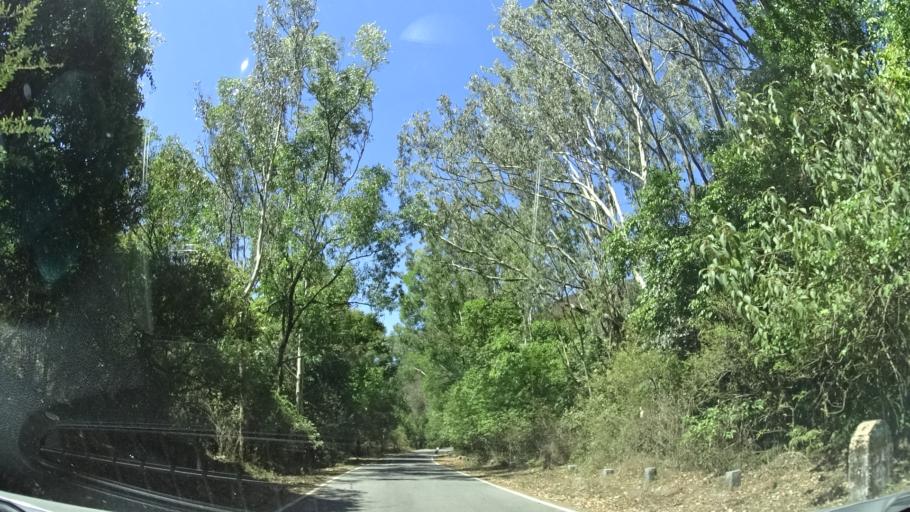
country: IN
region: Karnataka
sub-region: Chikmagalur
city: Sringeri
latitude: 13.2146
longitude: 75.2354
